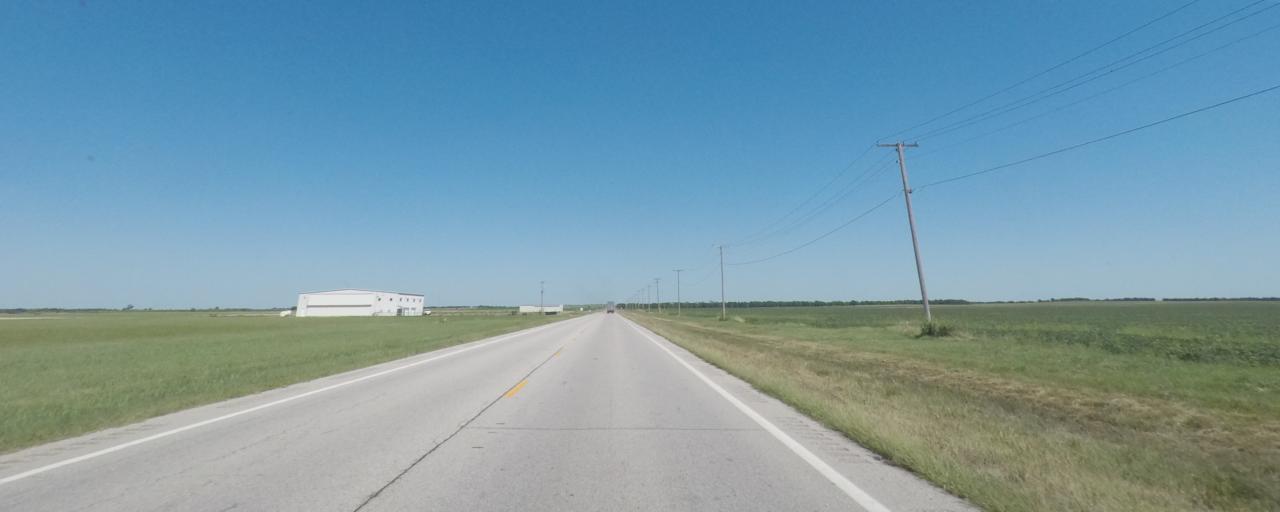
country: US
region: Kansas
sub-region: Sumner County
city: Wellington
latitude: 37.3265
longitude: -97.3849
